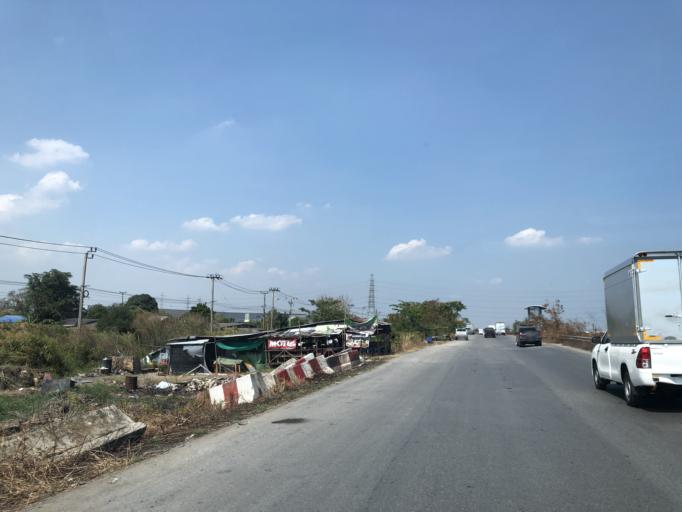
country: TH
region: Samut Prakan
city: Bang Bo District
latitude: 13.5755
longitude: 100.7572
